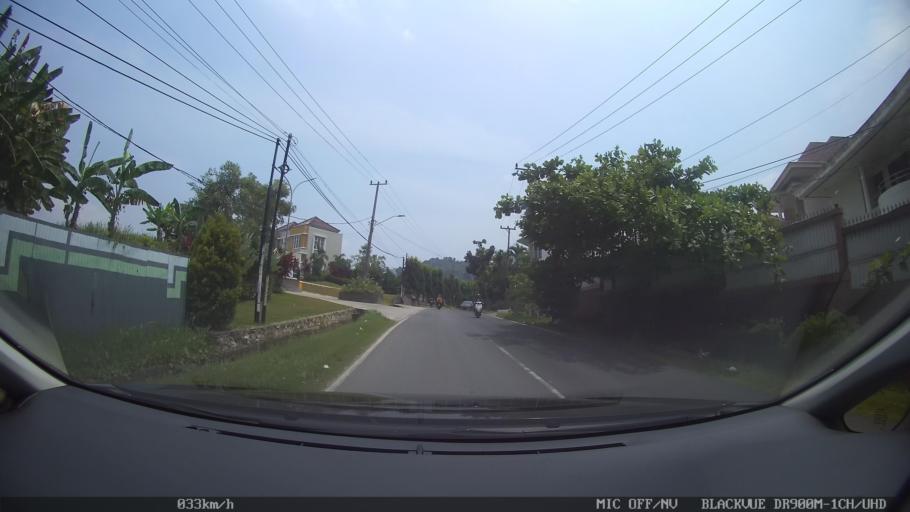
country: ID
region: Lampung
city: Bandarlampung
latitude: -5.4395
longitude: 105.2829
